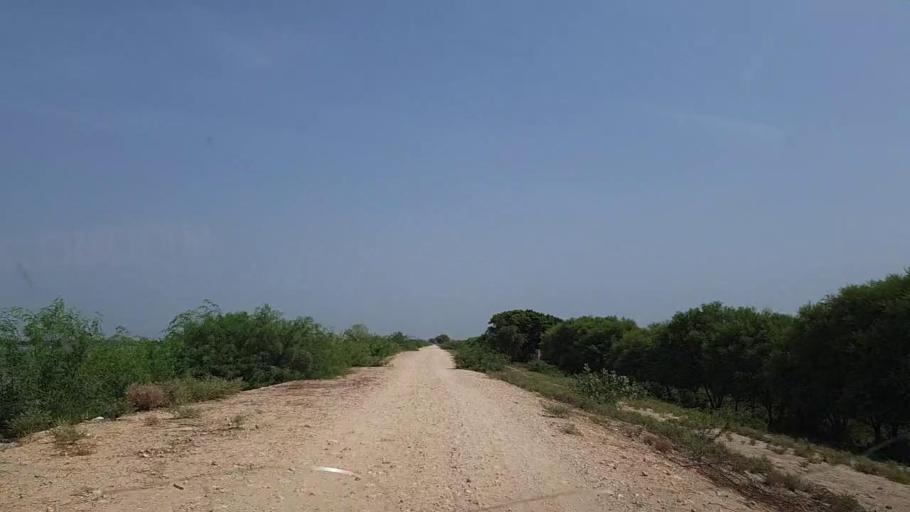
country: PK
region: Sindh
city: Ghotki
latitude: 28.0981
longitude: 69.4030
